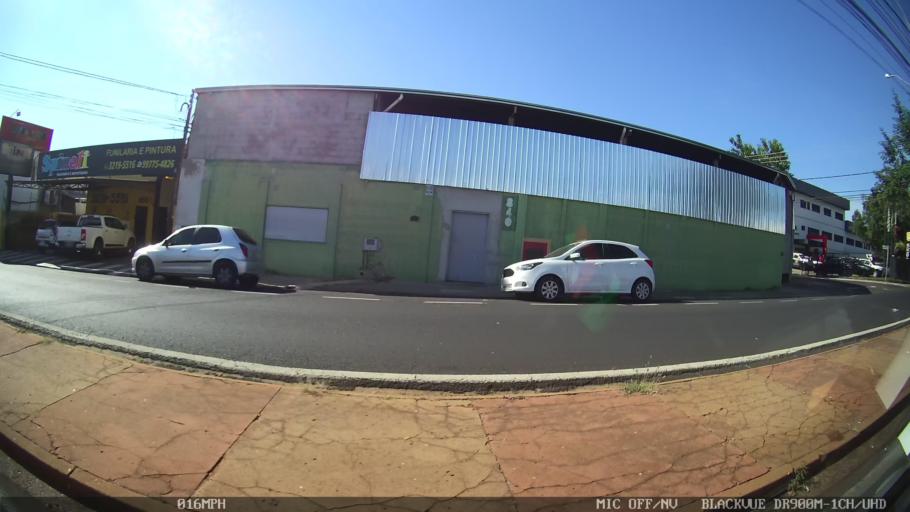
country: BR
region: Sao Paulo
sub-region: Sao Jose Do Rio Preto
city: Sao Jose do Rio Preto
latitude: -20.7819
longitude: -49.3868
